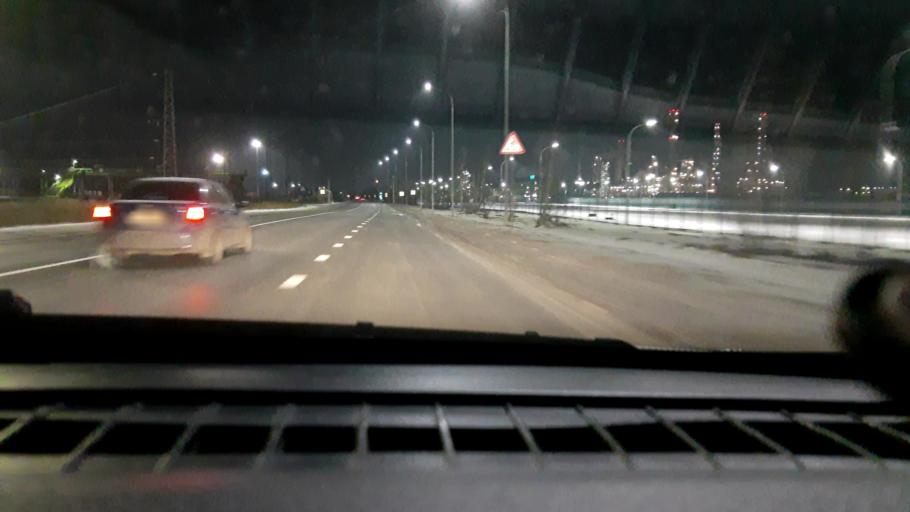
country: RU
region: Nizjnij Novgorod
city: Babino
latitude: 56.2532
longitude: 43.5814
